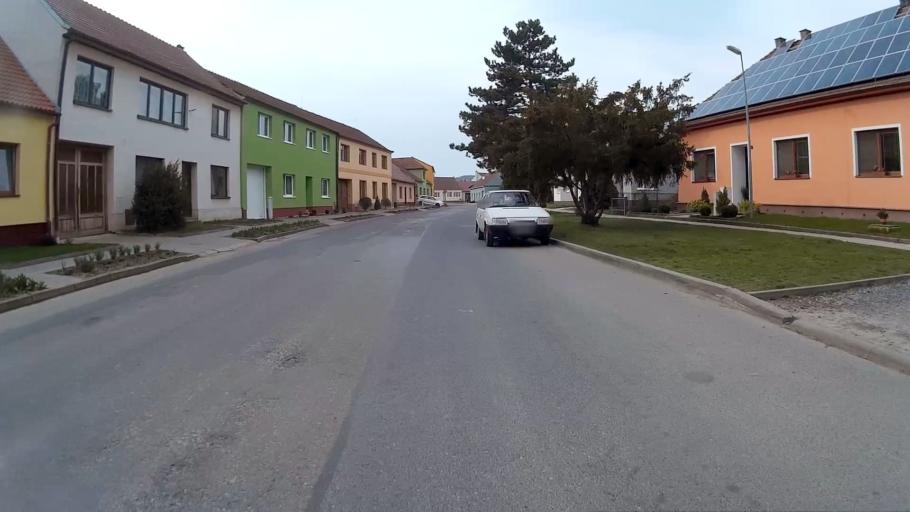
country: CZ
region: South Moravian
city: Dolni Kounice
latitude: 49.0711
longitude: 16.4420
